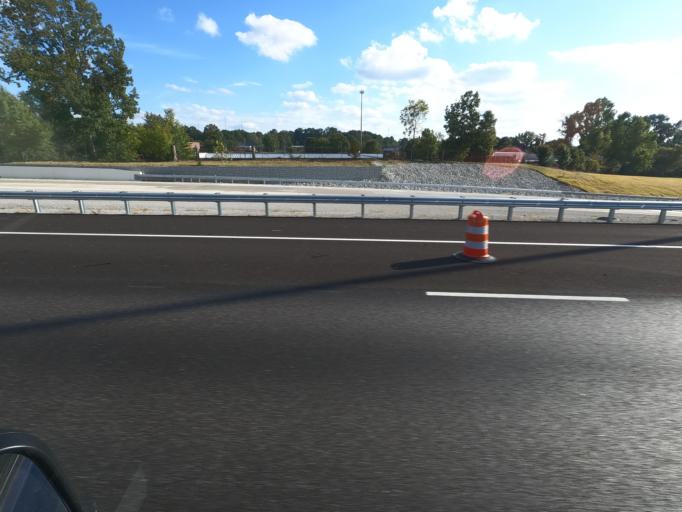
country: US
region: Tennessee
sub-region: Madison County
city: Jackson
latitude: 35.6725
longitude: -88.8270
